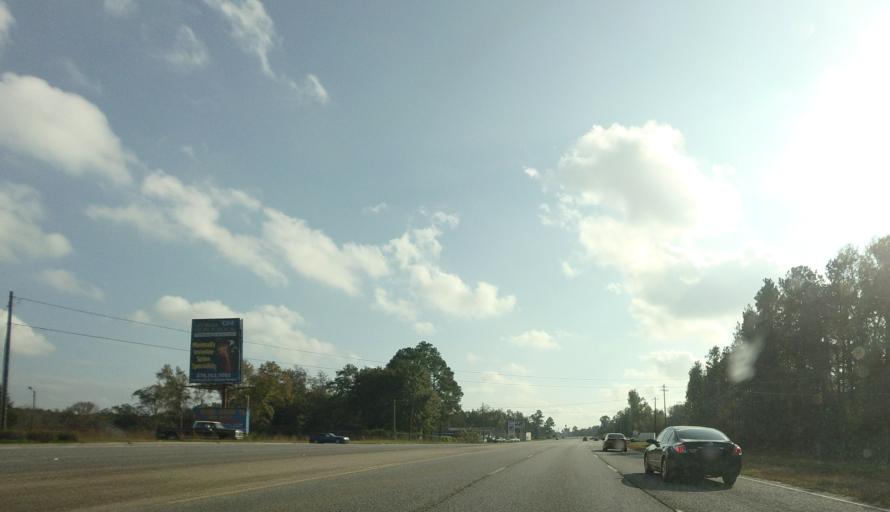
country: US
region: Georgia
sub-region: Bibb County
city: Macon
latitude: 32.7435
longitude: -83.6552
